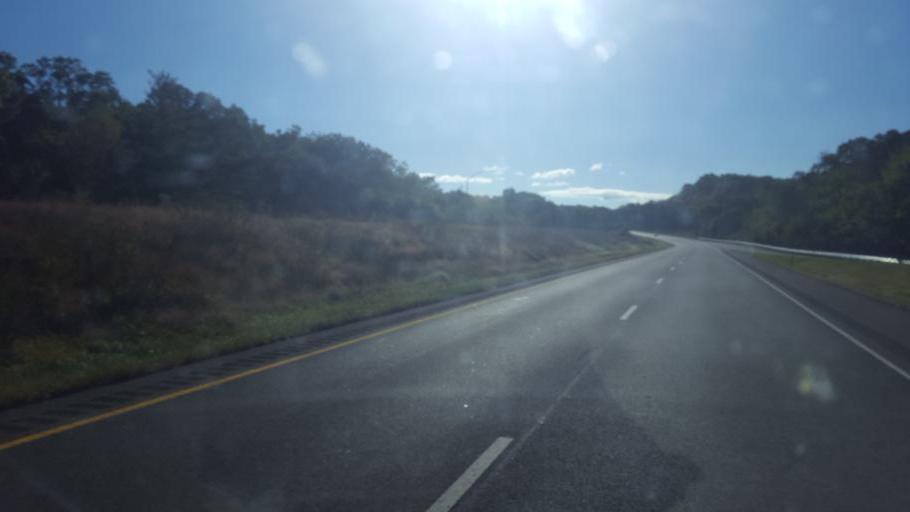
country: US
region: West Virginia
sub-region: Berkeley County
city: Martinsburg
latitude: 39.6273
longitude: -78.0156
